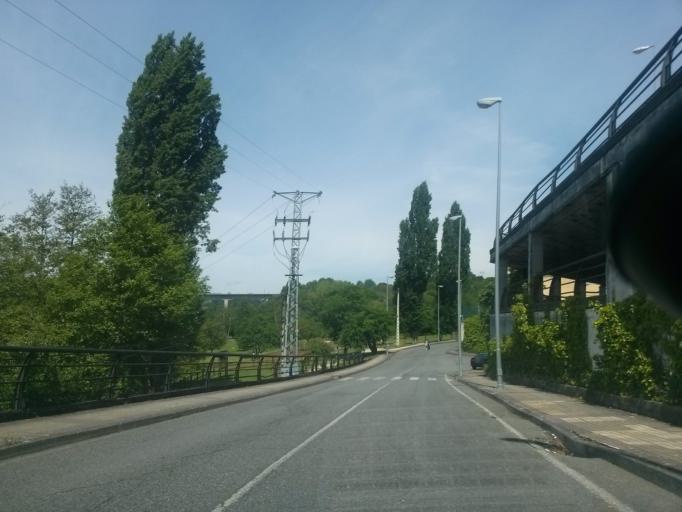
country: ES
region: Galicia
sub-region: Provincia de Lugo
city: Lugo
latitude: 43.0039
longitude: -7.5736
